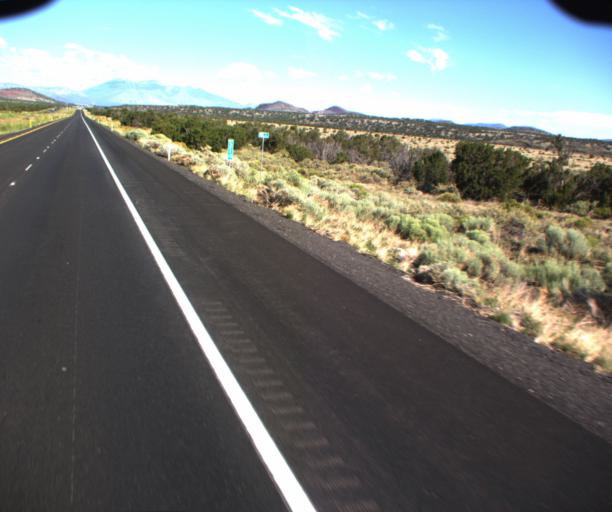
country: US
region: Arizona
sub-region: Coconino County
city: Flagstaff
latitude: 35.1837
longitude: -111.3619
